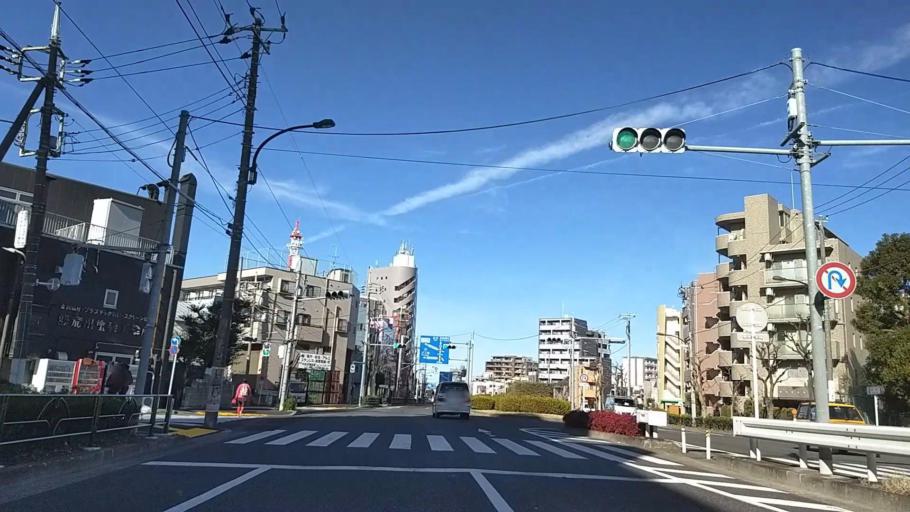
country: JP
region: Kanagawa
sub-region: Kawasaki-shi
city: Kawasaki
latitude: 35.5699
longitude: 139.6904
